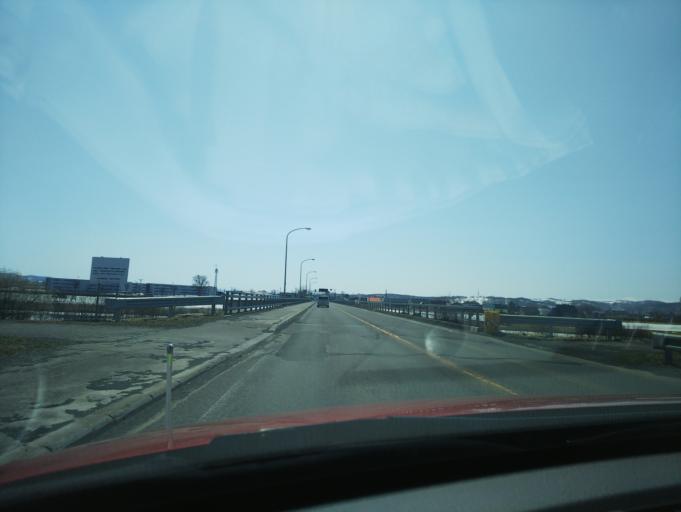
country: JP
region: Hokkaido
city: Nayoro
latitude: 44.1929
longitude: 142.3940
